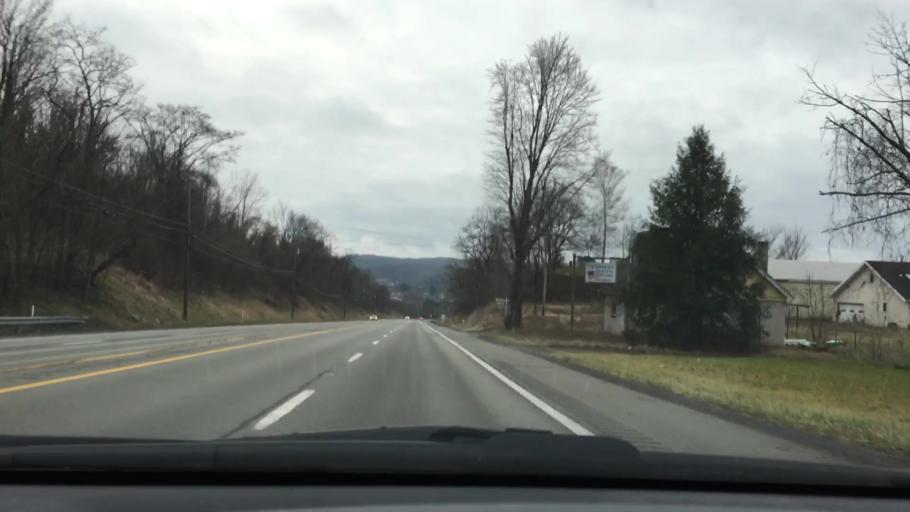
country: US
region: Pennsylvania
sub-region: Fayette County
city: Perryopolis
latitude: 40.1016
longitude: -79.7664
